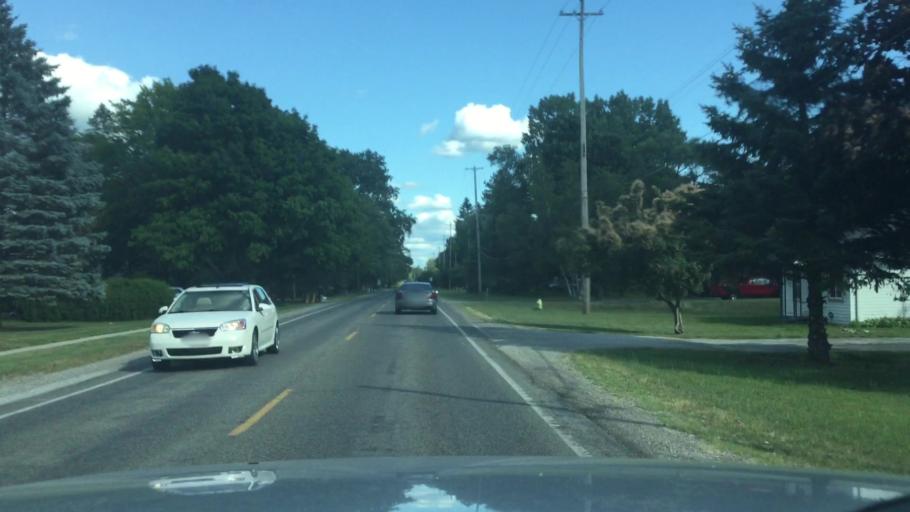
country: US
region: Michigan
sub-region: Saginaw County
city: Bridgeport
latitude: 43.3697
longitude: -83.9014
